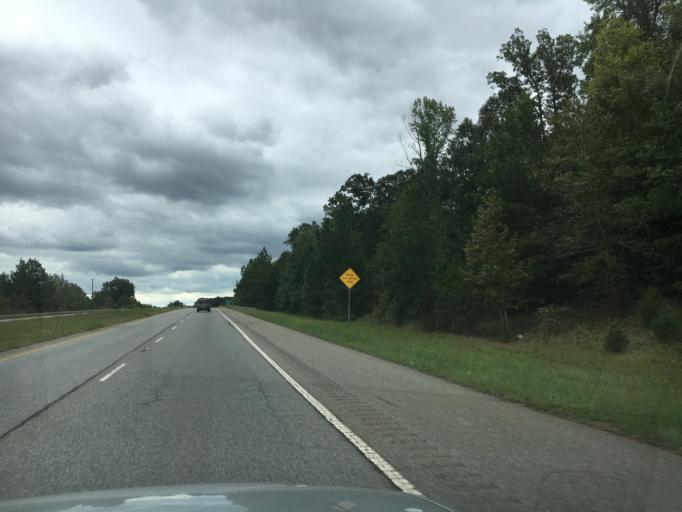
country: US
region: South Carolina
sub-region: Greenville County
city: Golden Grove
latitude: 34.7210
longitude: -82.3699
